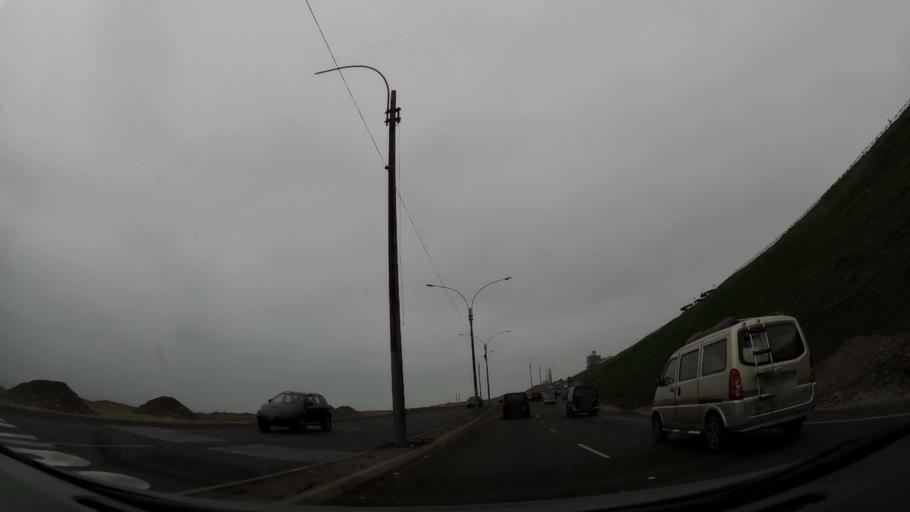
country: PE
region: Callao
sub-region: Callao
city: Callao
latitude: -12.0897
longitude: -77.0895
